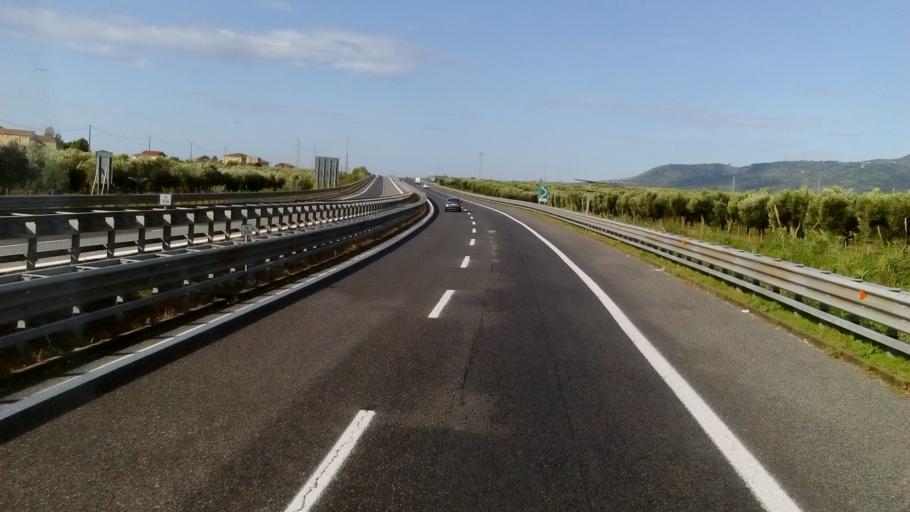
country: IT
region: Calabria
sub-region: Provincia di Catanzaro
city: Santa Eufemia Lamezia
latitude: 38.9235
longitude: 16.2591
